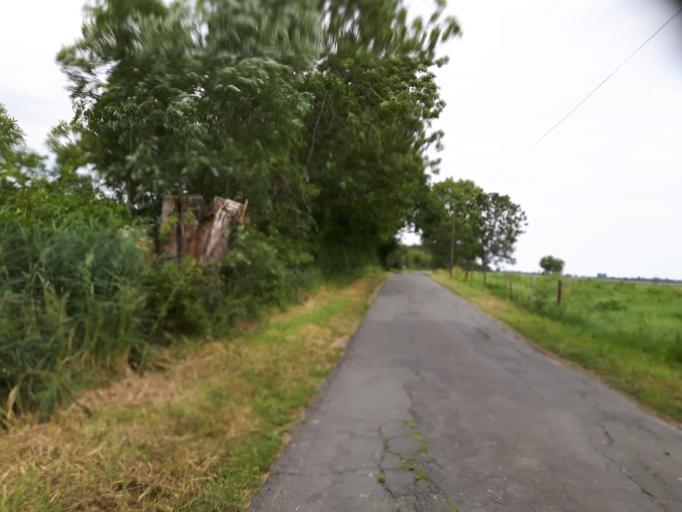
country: DE
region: Lower Saxony
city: Varel
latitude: 53.3623
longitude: 8.2053
